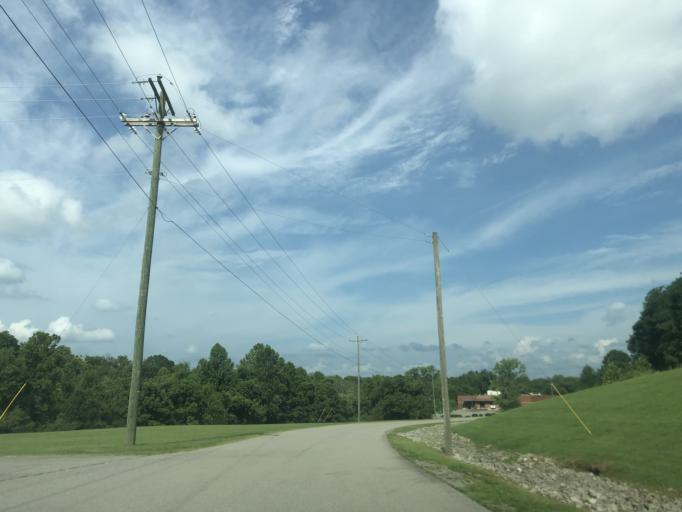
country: US
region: Tennessee
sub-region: Davidson County
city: Lakewood
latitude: 36.1672
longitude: -86.6451
